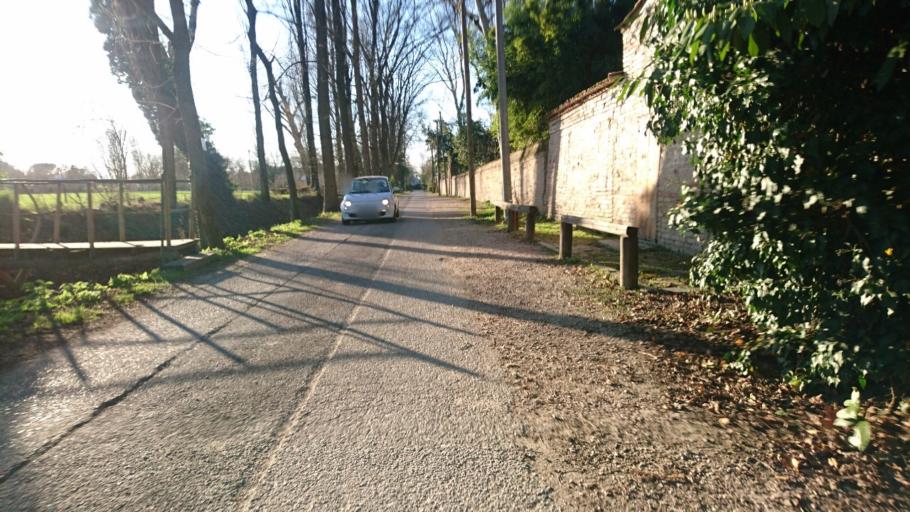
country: IT
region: Veneto
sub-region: Provincia di Padova
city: Bertipaglia
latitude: 45.3027
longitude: 11.8858
